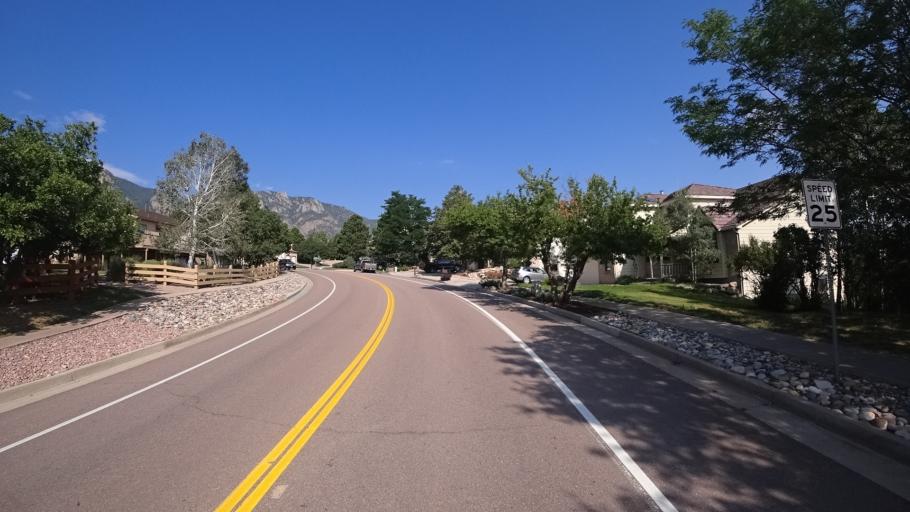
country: US
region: Colorado
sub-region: El Paso County
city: Fort Carson
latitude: 38.7572
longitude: -104.8267
